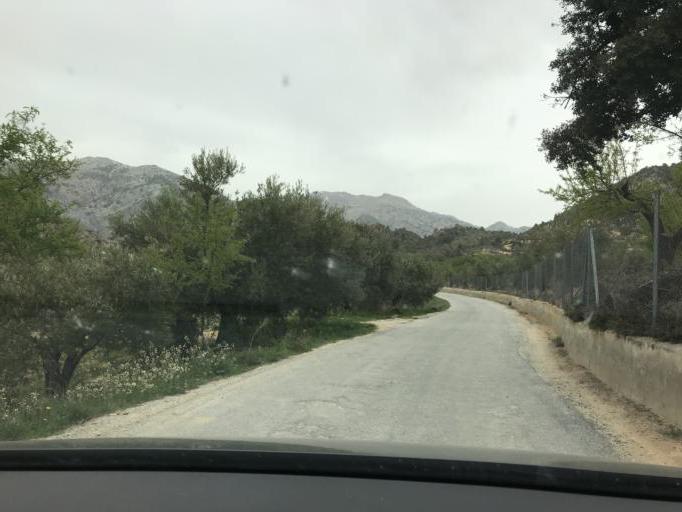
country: ES
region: Andalusia
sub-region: Provincia de Granada
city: Castril
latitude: 37.8201
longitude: -2.7674
